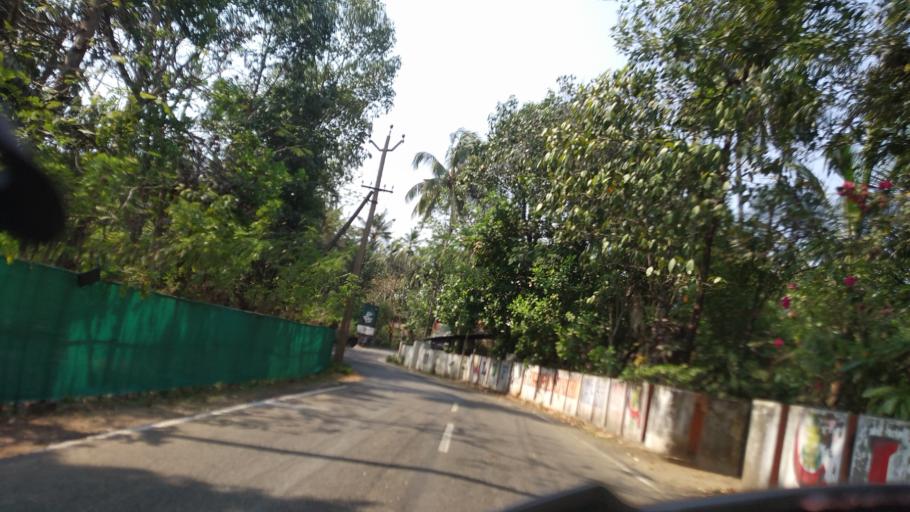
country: IN
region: Kerala
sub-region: Thrissur District
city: Thanniyam
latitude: 10.3677
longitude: 76.1062
